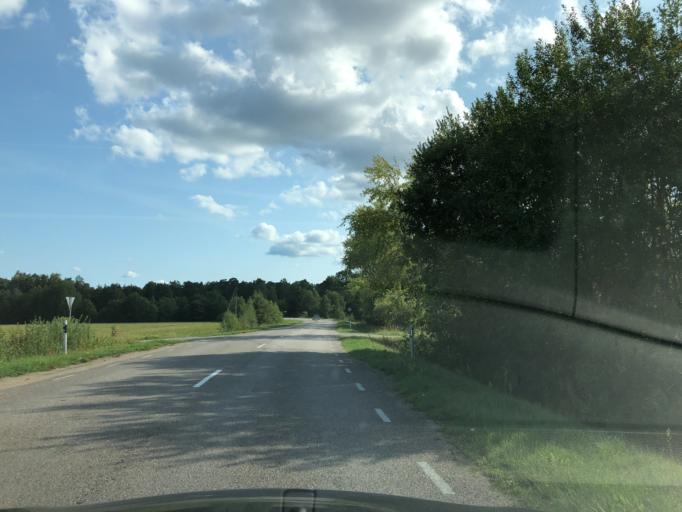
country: EE
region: Hiiumaa
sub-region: Kaerdla linn
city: Kardla
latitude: 58.7105
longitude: 22.5869
